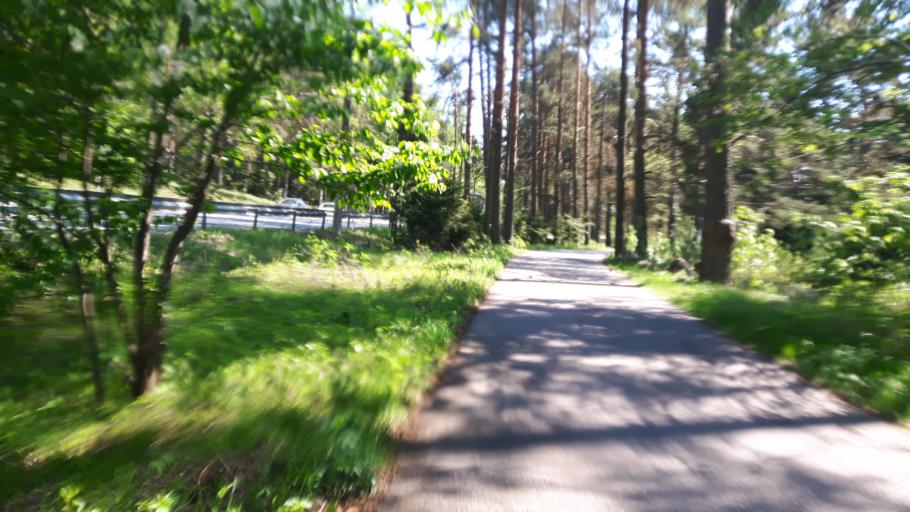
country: RU
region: St.-Petersburg
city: Komarovo
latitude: 60.1796
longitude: 29.7787
